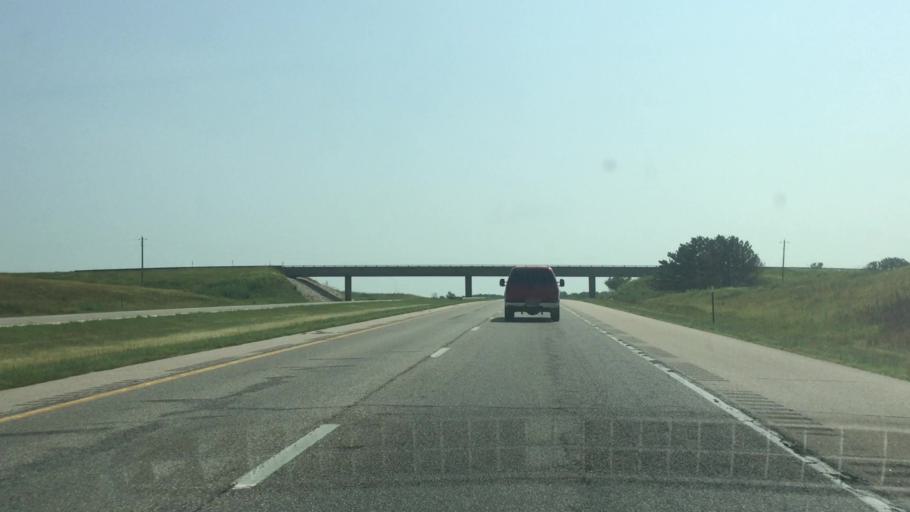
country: US
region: Kansas
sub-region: Osage County
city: Lyndon
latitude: 38.4262
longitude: -95.7868
